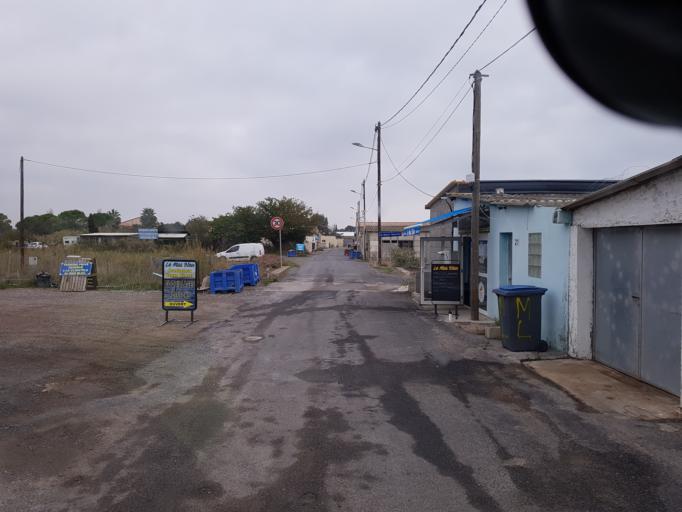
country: FR
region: Languedoc-Roussillon
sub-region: Departement de l'Herault
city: Marseillan
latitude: 43.3630
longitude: 3.5364
